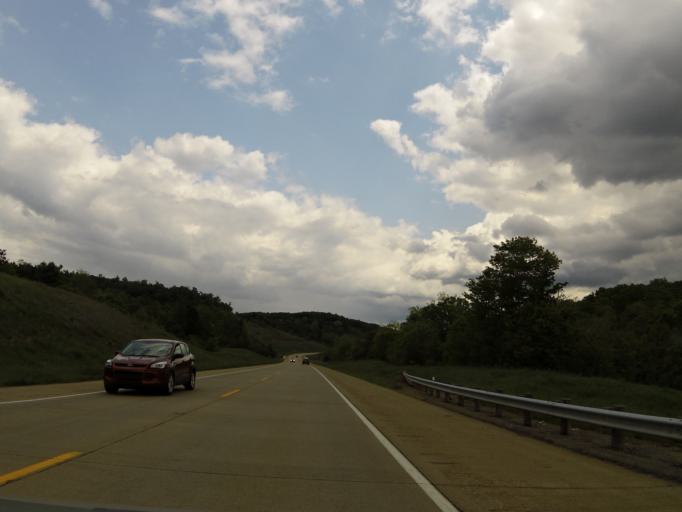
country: US
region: West Virginia
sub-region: Jackson County
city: Ravenswood
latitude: 38.9658
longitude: -81.8342
